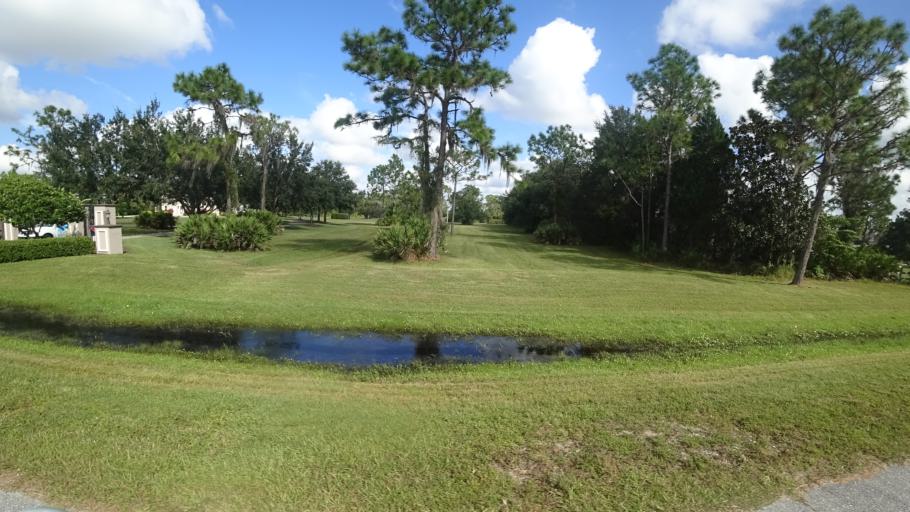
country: US
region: Florida
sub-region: Sarasota County
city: The Meadows
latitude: 27.3984
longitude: -82.3348
